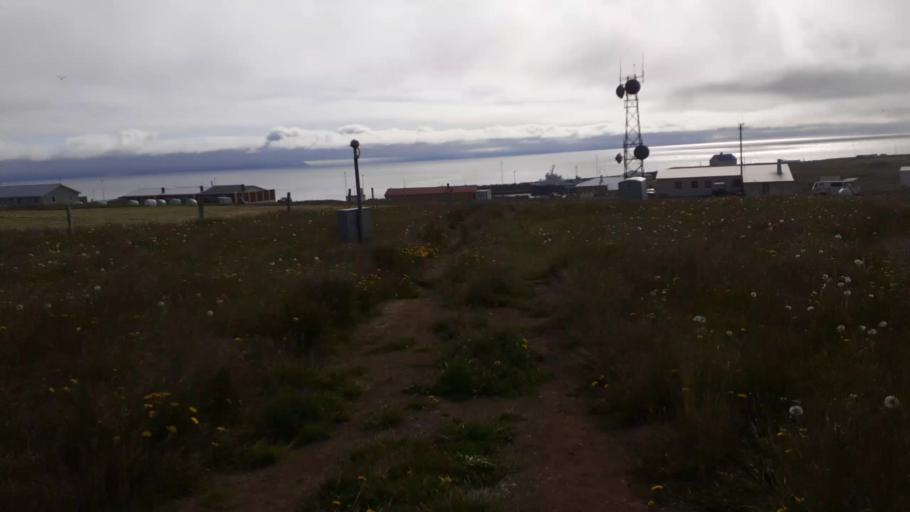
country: IS
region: Northeast
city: Dalvik
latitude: 66.5411
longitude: -18.0125
